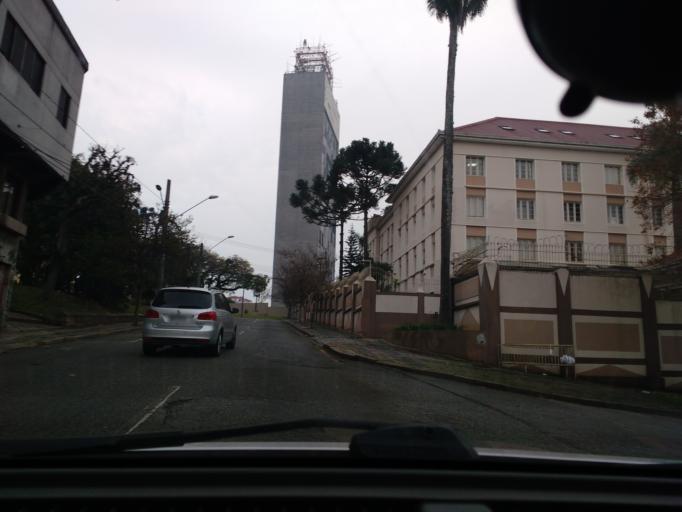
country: BR
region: Parana
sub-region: Curitiba
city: Curitiba
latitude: -25.4244
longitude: -49.2786
